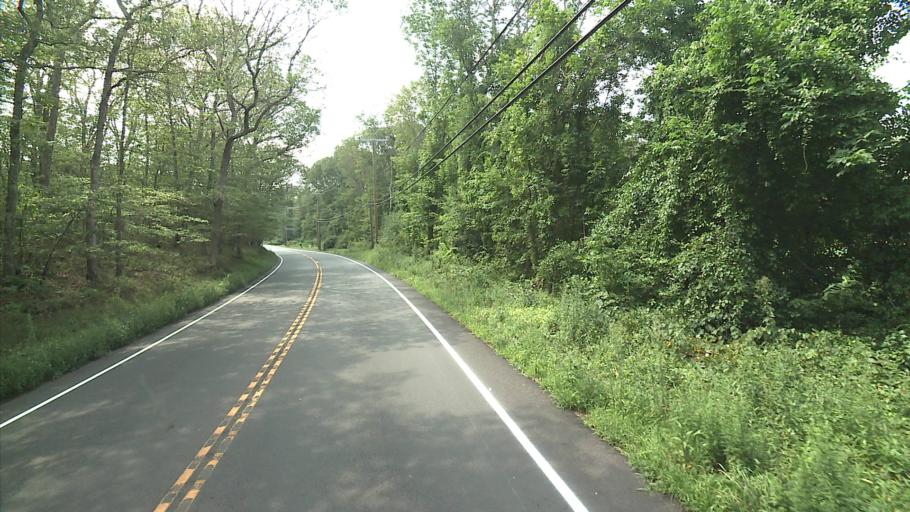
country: US
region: Connecticut
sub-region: New London County
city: Montville Center
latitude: 41.4880
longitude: -72.2493
